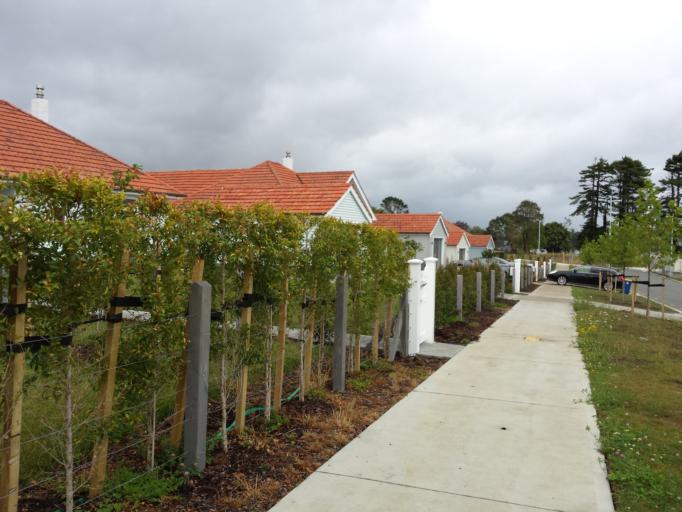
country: NZ
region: Auckland
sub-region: Auckland
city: Rosebank
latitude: -36.7889
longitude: 174.6640
